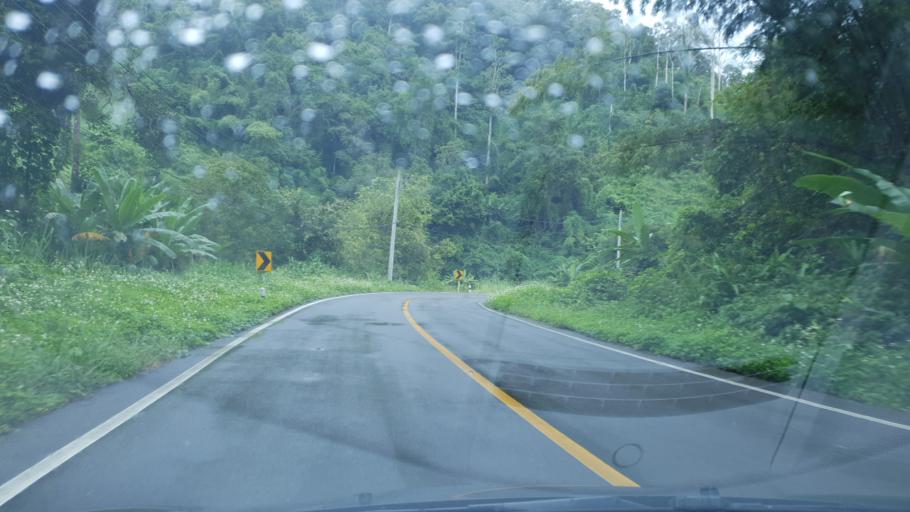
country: TH
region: Mae Hong Son
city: Mae La Noi
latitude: 18.5845
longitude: 97.9414
